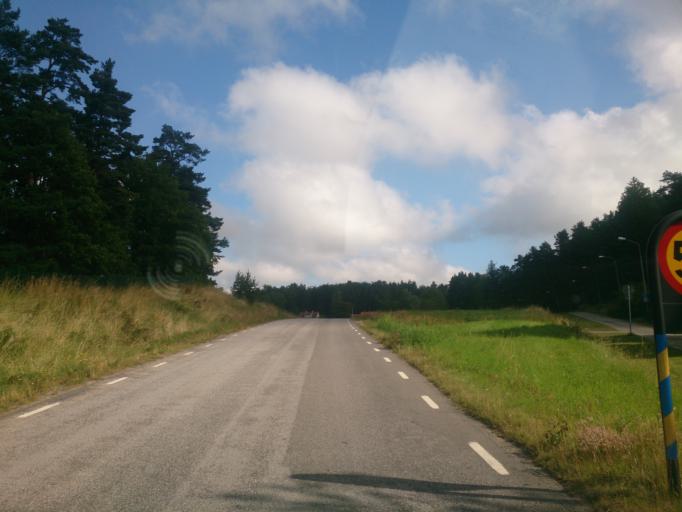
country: SE
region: OEstergoetland
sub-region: Linkopings Kommun
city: Sturefors
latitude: 58.3022
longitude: 15.8652
